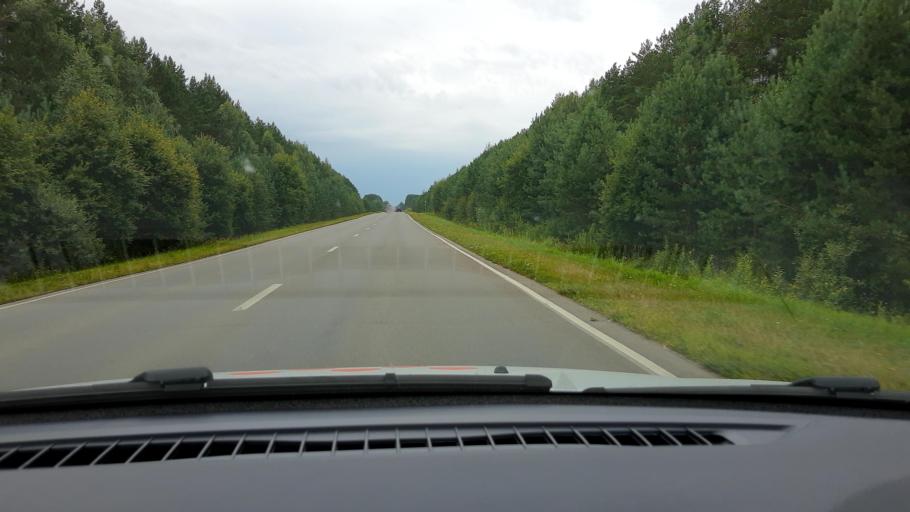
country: RU
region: Nizjnij Novgorod
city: Vyyezdnoye
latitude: 55.1661
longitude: 43.5893
